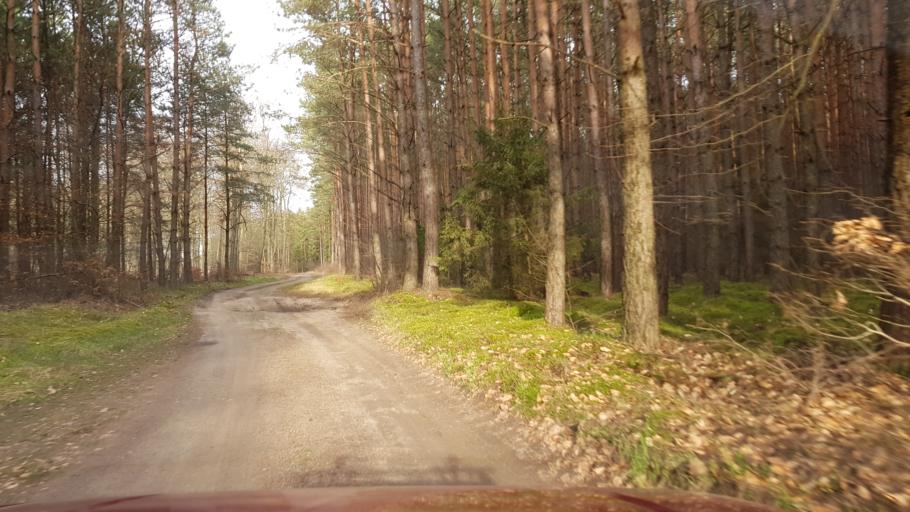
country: PL
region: Lubusz
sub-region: Powiat strzelecko-drezdenecki
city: Strzelce Krajenskie
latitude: 52.9134
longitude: 15.4108
